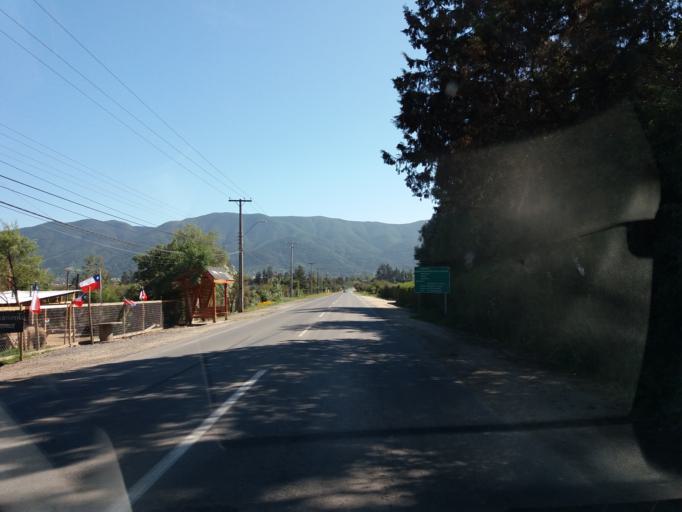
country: CL
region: Valparaiso
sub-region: Provincia de Marga Marga
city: Limache
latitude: -33.0171
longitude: -71.1716
